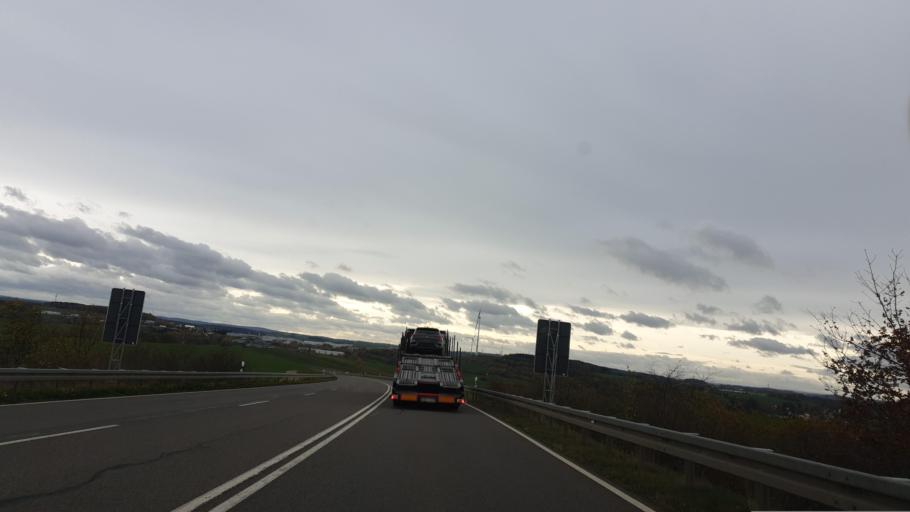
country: DE
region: Saxony
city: Reichenbach/Vogtland
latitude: 50.6235
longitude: 12.3343
